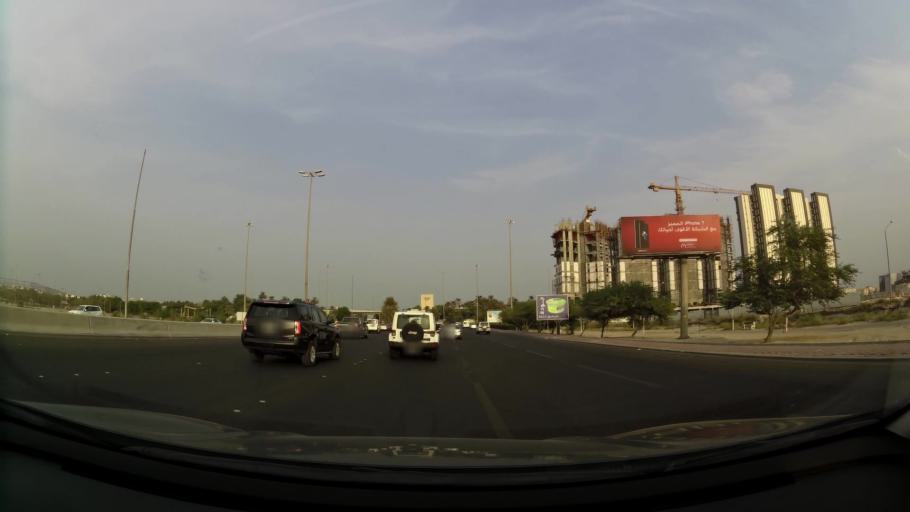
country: KW
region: Mubarak al Kabir
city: Sabah as Salim
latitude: 29.2677
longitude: 48.0817
